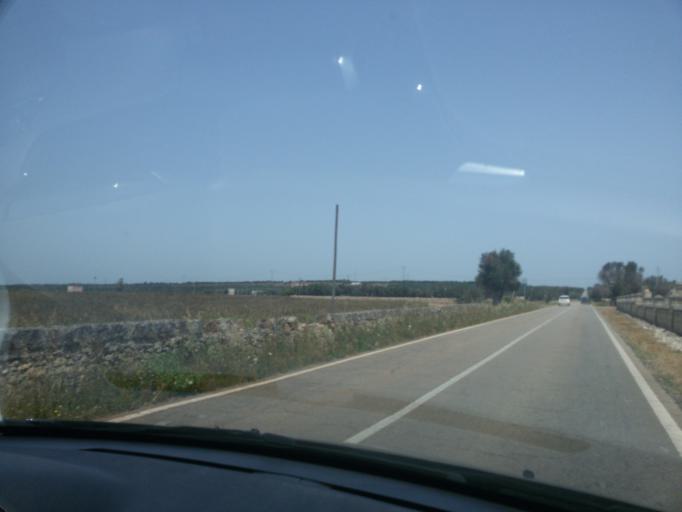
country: IT
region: Apulia
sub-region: Provincia di Lecce
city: Porto Cesareo
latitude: 40.2836
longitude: 17.9084
